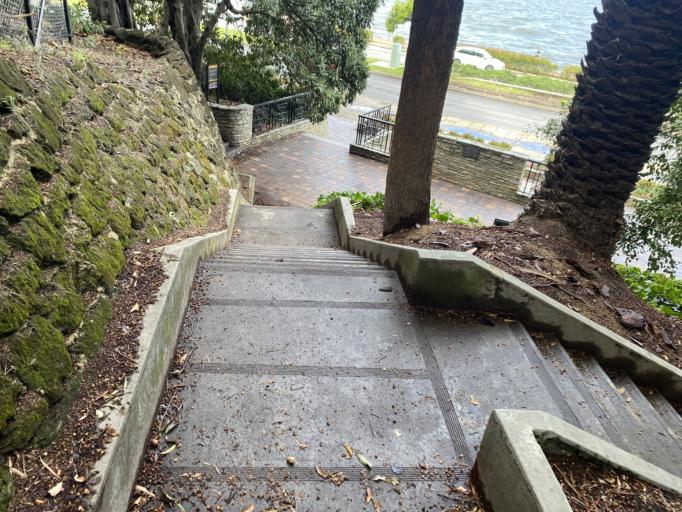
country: AU
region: Western Australia
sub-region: City of Perth
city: West Perth
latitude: -31.9626
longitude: 115.8429
